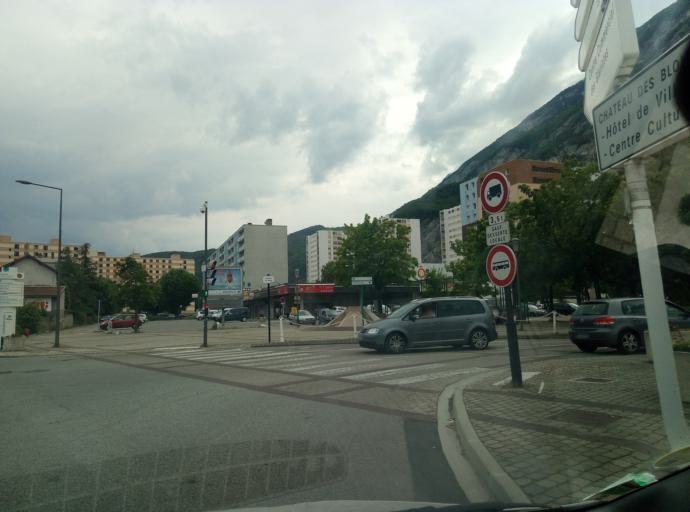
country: FR
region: Rhone-Alpes
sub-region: Departement de l'Isere
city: Sassenage
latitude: 45.2051
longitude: 5.6642
